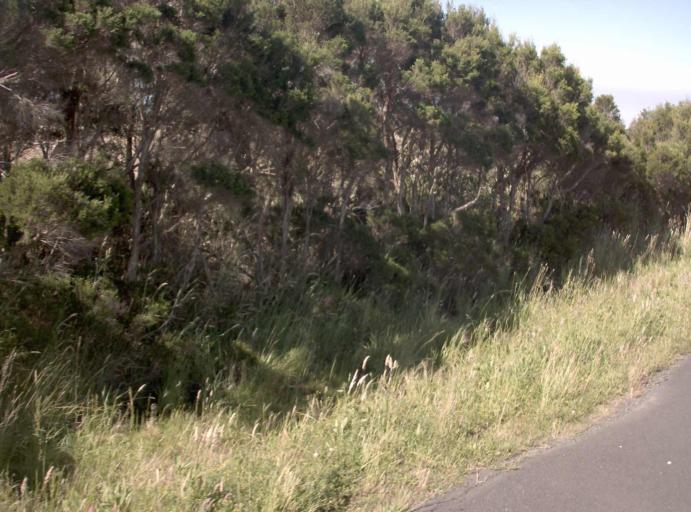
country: AU
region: Victoria
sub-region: Latrobe
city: Traralgon
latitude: -38.6273
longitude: 146.6220
